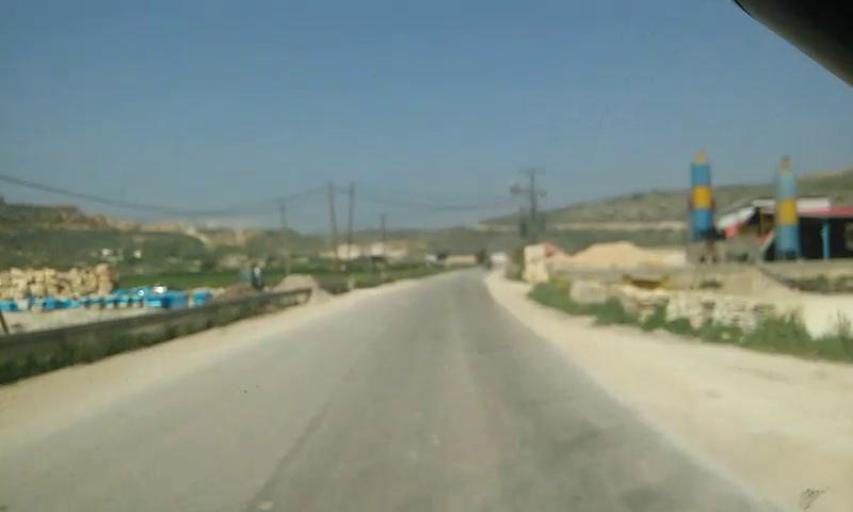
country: PS
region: West Bank
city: Az Zababidah
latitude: 32.3970
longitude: 35.3194
